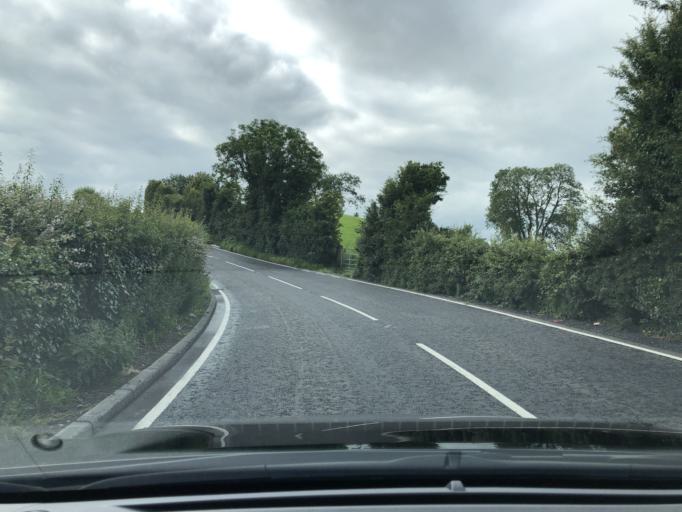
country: GB
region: Northern Ireland
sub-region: Down District
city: Dundrum
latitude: 54.2870
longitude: -5.8285
